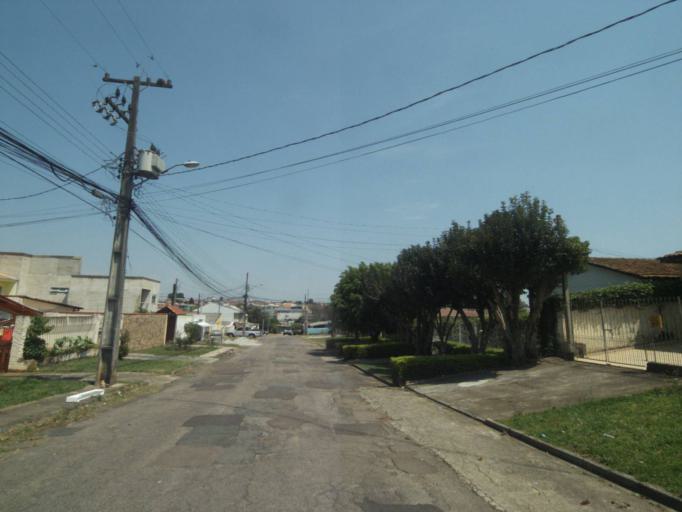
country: BR
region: Parana
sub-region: Sao Jose Dos Pinhais
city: Sao Jose dos Pinhais
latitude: -25.5174
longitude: -49.2688
